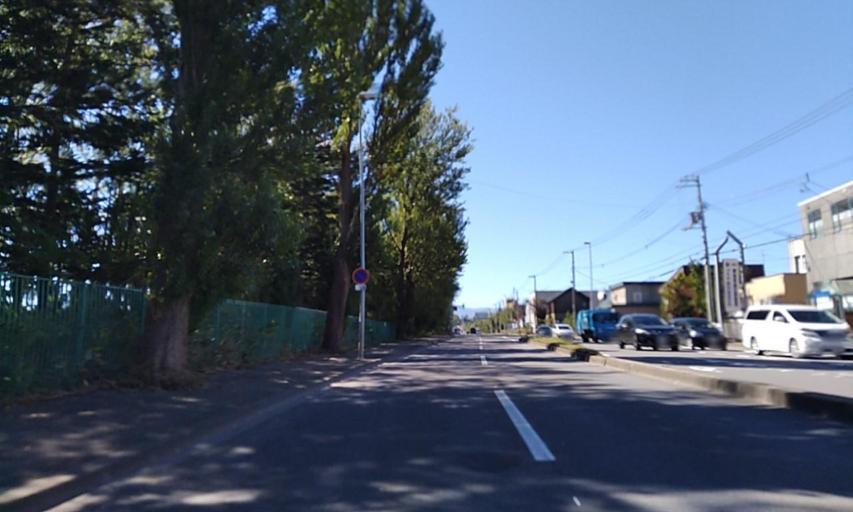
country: JP
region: Hokkaido
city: Sapporo
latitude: 43.0128
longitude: 141.4037
